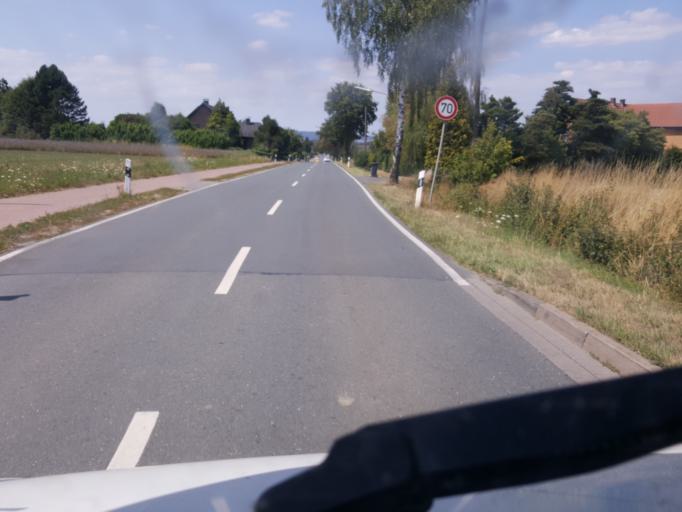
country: DE
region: North Rhine-Westphalia
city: Bad Oeynhausen
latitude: 52.2289
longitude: 8.7633
